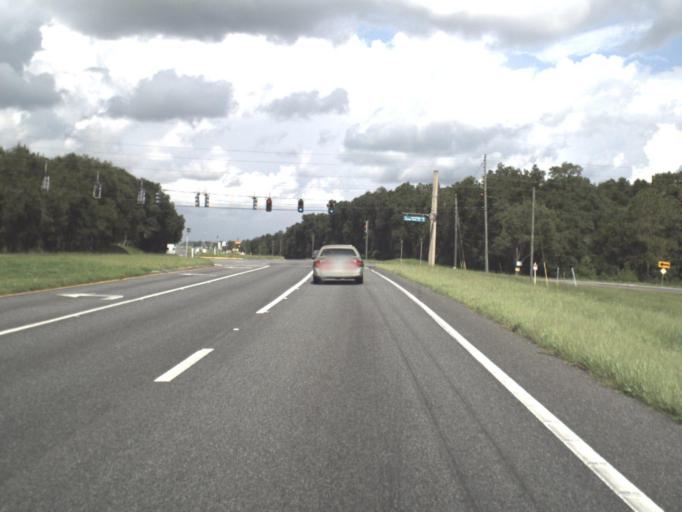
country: US
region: Florida
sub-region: Hernando County
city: Ridge Manor
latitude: 28.5229
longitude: -82.2191
